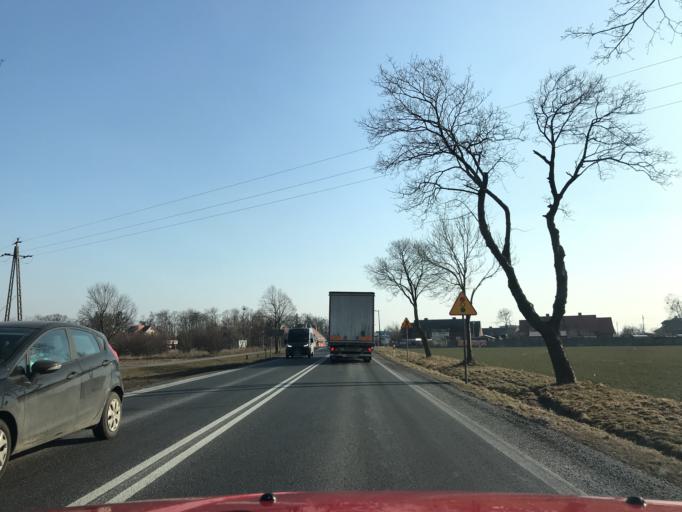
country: PL
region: Greater Poland Voivodeship
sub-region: Powiat sredzki
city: Nowe Miasto nad Warta
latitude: 52.0773
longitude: 17.4179
